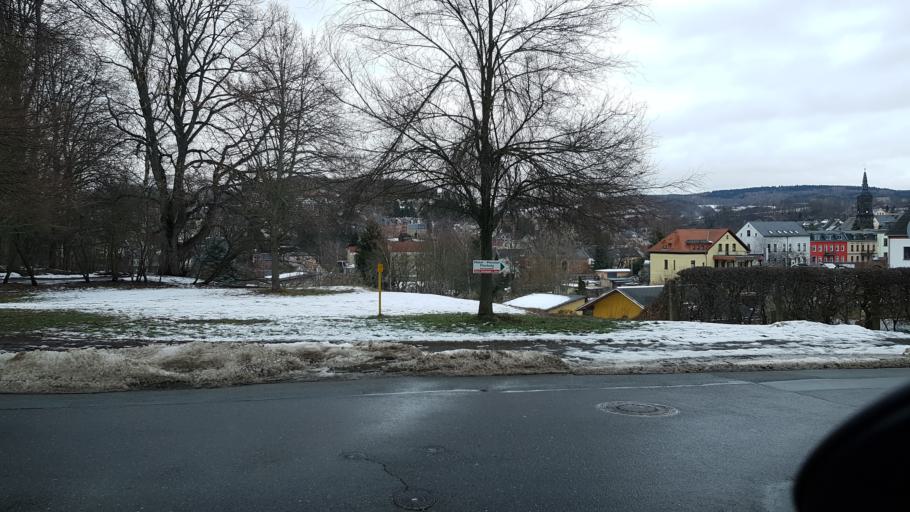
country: DE
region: Saxony
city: Kirchberg
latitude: 50.6225
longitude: 12.5190
